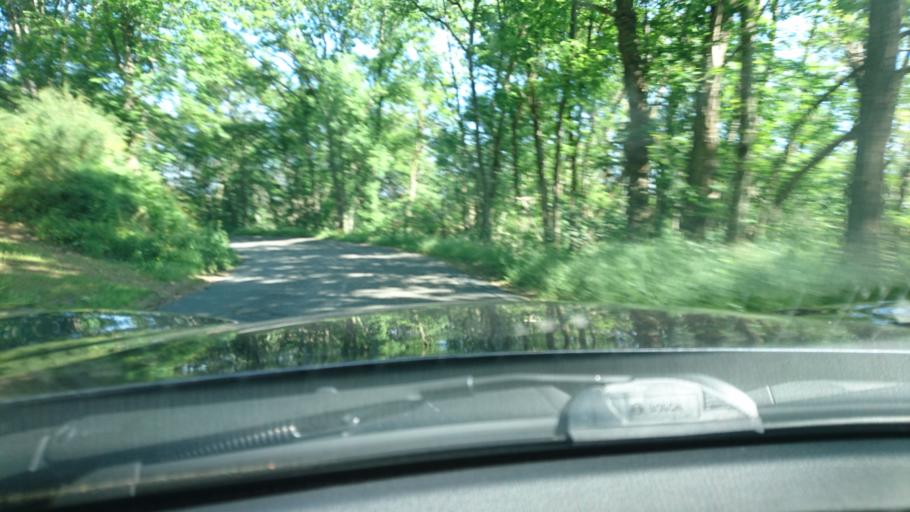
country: FR
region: Rhone-Alpes
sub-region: Departement du Rhone
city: Saint-Pierre-la-Palud
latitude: 45.7646
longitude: 4.6100
